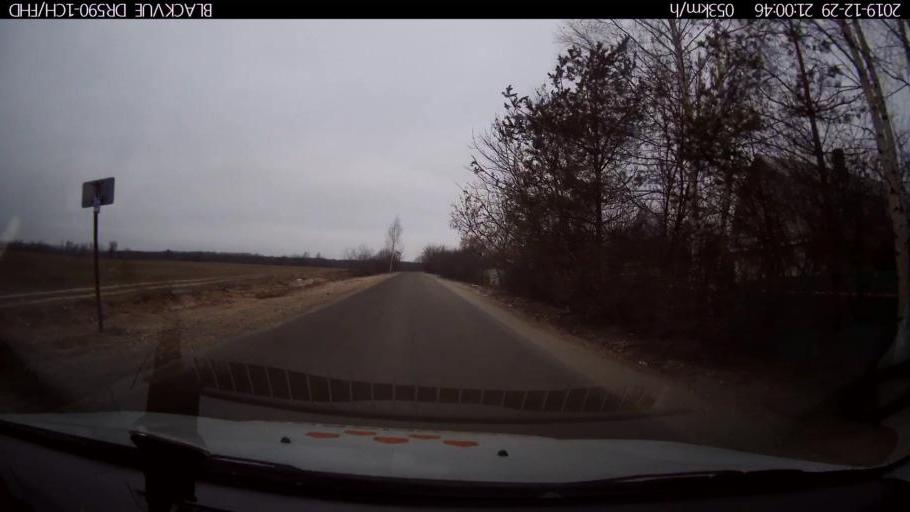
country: RU
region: Nizjnij Novgorod
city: Afonino
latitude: 56.1842
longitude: 43.9904
